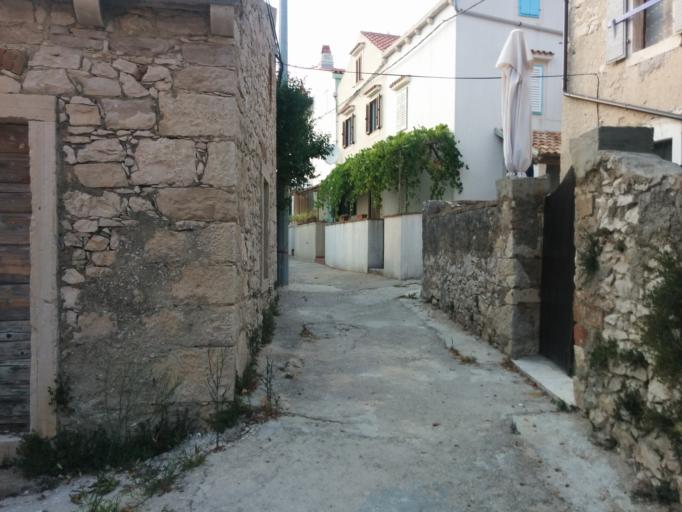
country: HR
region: Primorsko-Goranska
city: Mali Losinj
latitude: 44.6367
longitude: 14.2482
